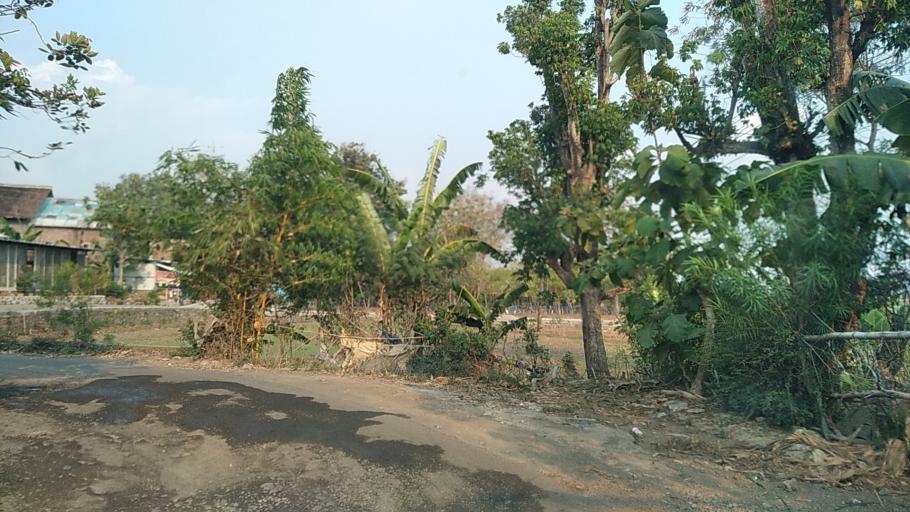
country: ID
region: Central Java
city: Mranggen
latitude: -7.0618
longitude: 110.4854
